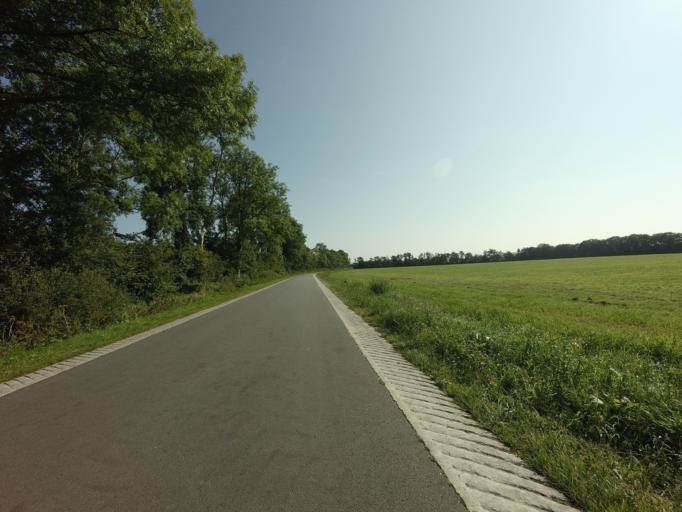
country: NL
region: Drenthe
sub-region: Gemeente Tynaarlo
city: Vries
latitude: 53.0901
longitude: 6.5347
